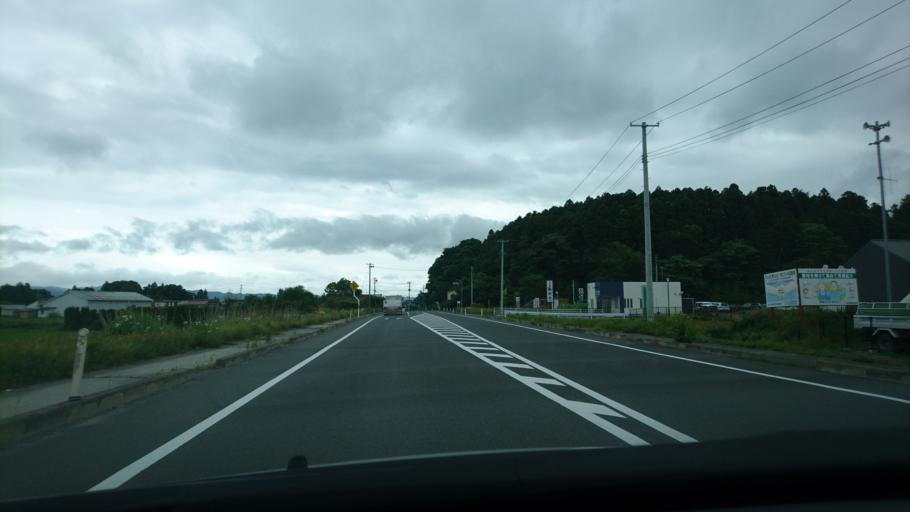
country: JP
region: Iwate
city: Ichinoseki
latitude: 38.7343
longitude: 141.2590
